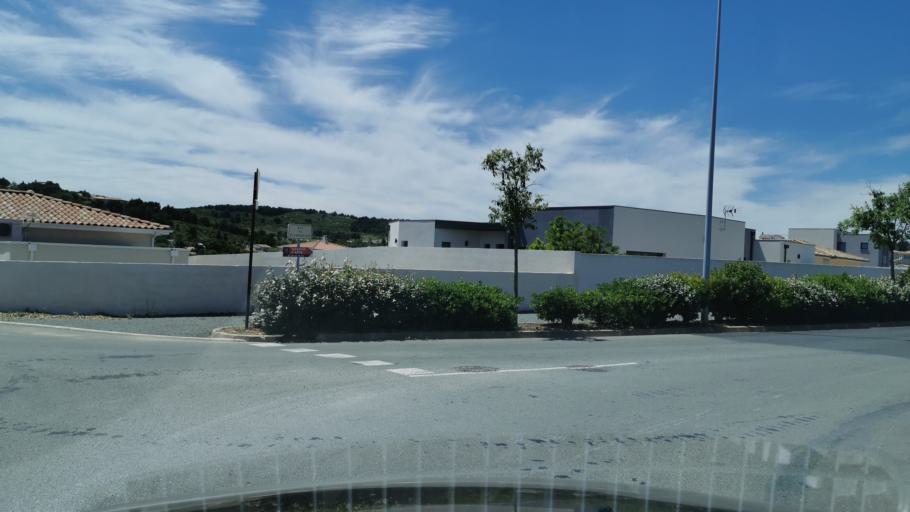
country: FR
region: Languedoc-Roussillon
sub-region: Departement de l'Aude
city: Narbonne
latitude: 43.1962
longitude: 2.9720
